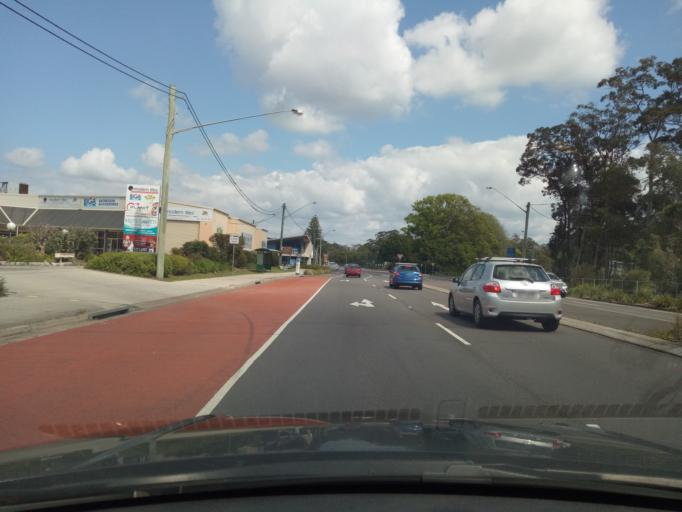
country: AU
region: New South Wales
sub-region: Gosford Shire
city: Erina
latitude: -33.4273
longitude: 151.3959
